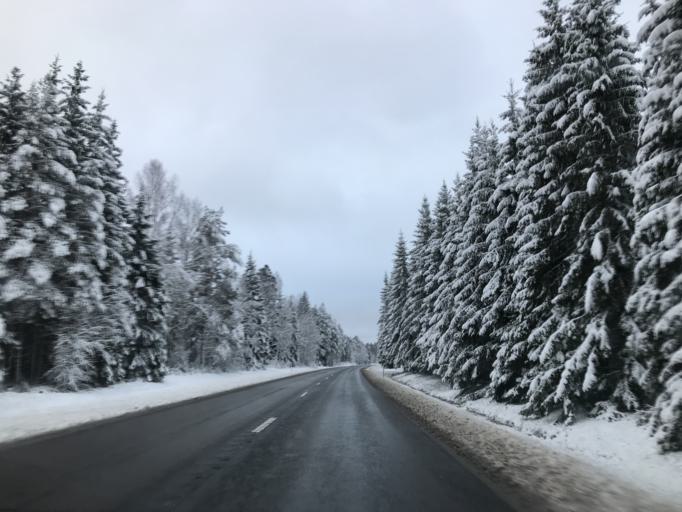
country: SE
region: Vaestra Goetaland
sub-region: Svenljunga Kommun
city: Svenljunga
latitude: 57.4563
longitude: 13.1149
